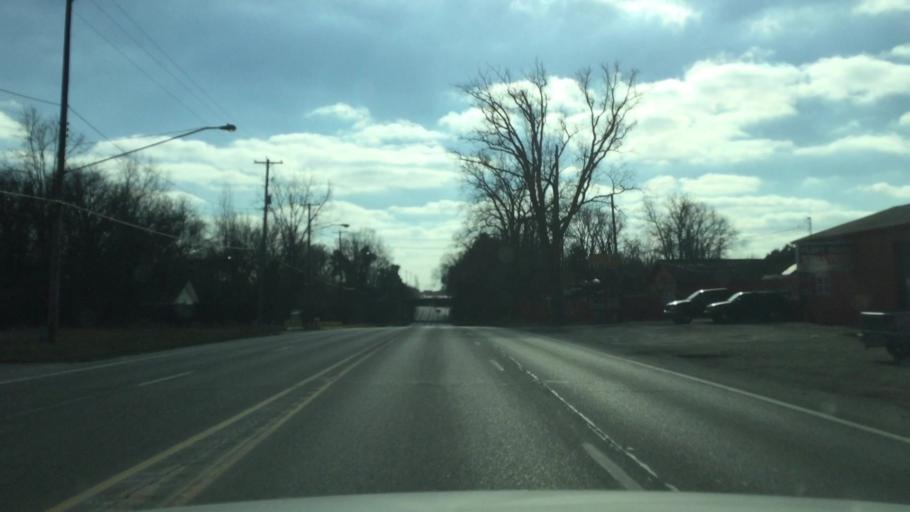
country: US
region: Michigan
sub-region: Genesee County
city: Beecher
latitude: 43.0668
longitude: -83.6741
